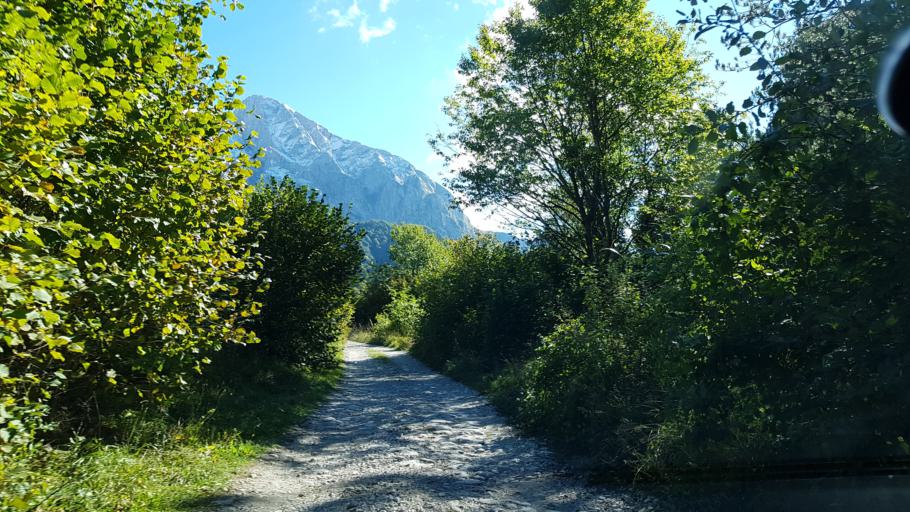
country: SI
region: Kobarid
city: Kobarid
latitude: 46.2751
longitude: 13.6174
